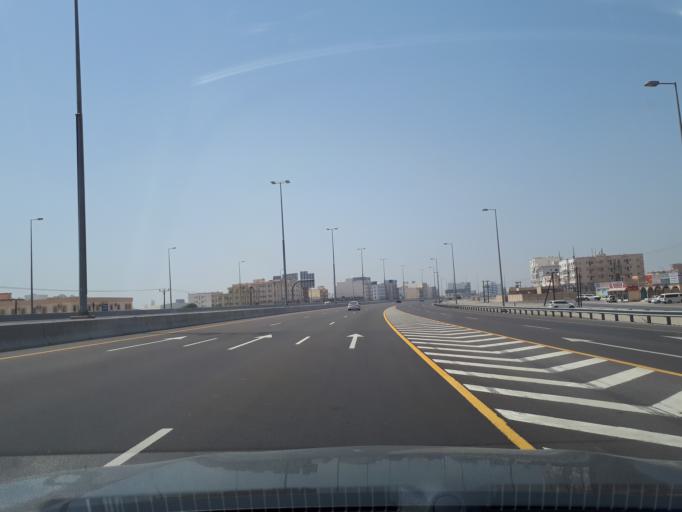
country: OM
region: Al Batinah
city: Al Liwa'
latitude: 24.4287
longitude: 56.6081
